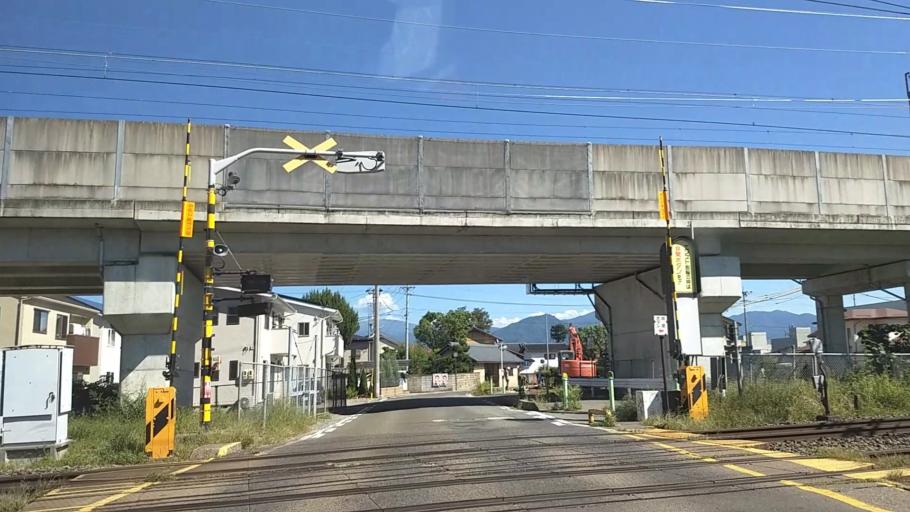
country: JP
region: Nagano
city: Nagano-shi
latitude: 36.6163
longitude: 138.1510
